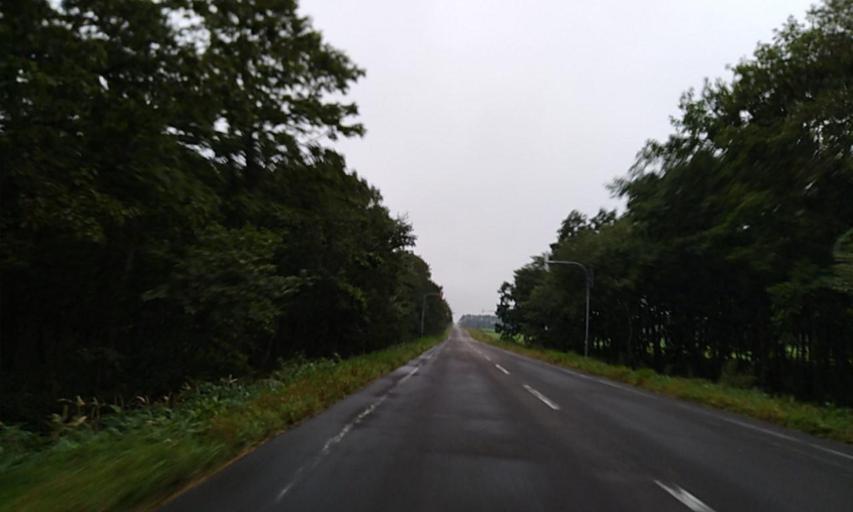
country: JP
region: Hokkaido
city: Shibetsu
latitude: 43.5188
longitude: 144.6826
